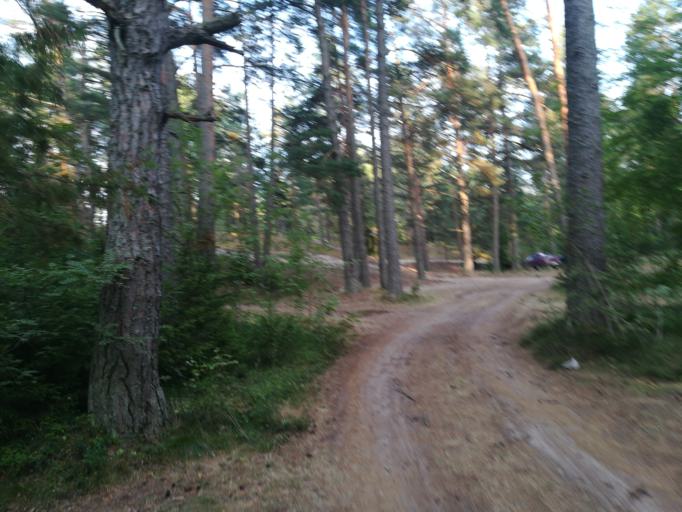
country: RU
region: Leningrad
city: Ust'-Luga
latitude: 59.6779
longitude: 28.2388
